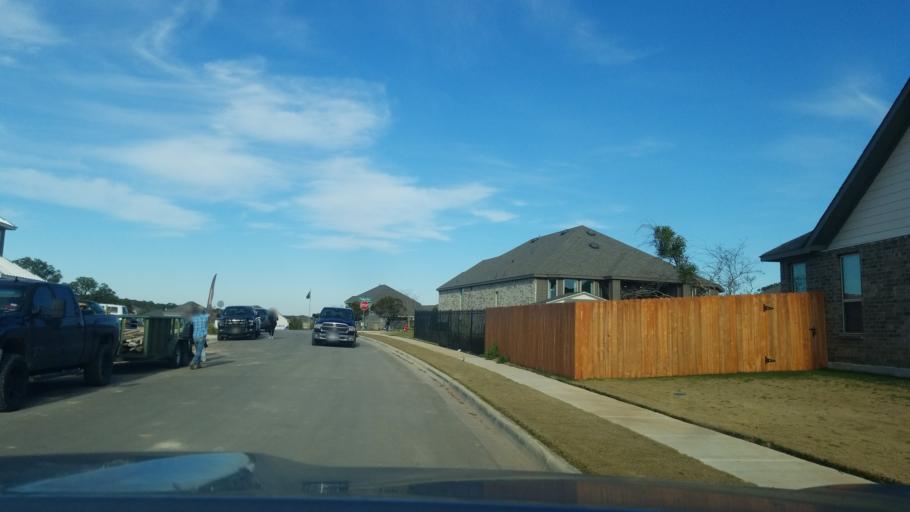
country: US
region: Texas
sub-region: Comal County
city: Canyon Lake
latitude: 29.7765
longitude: -98.2873
